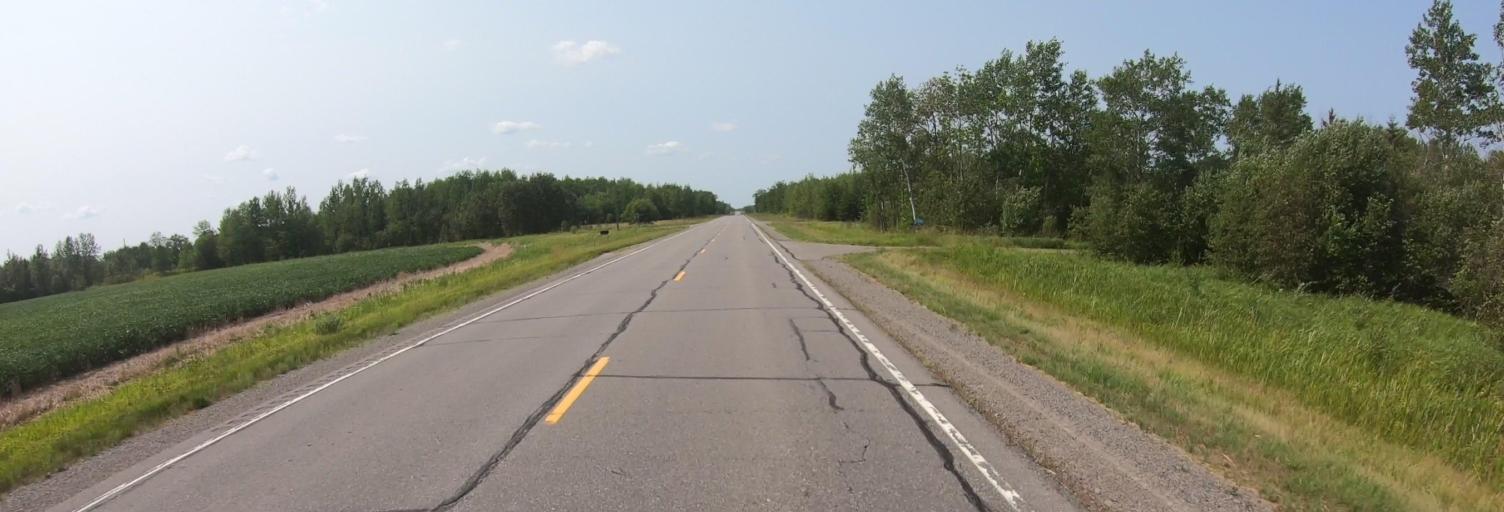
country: US
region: Minnesota
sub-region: Lake of the Woods County
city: Baudette
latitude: 48.6995
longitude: -94.3521
